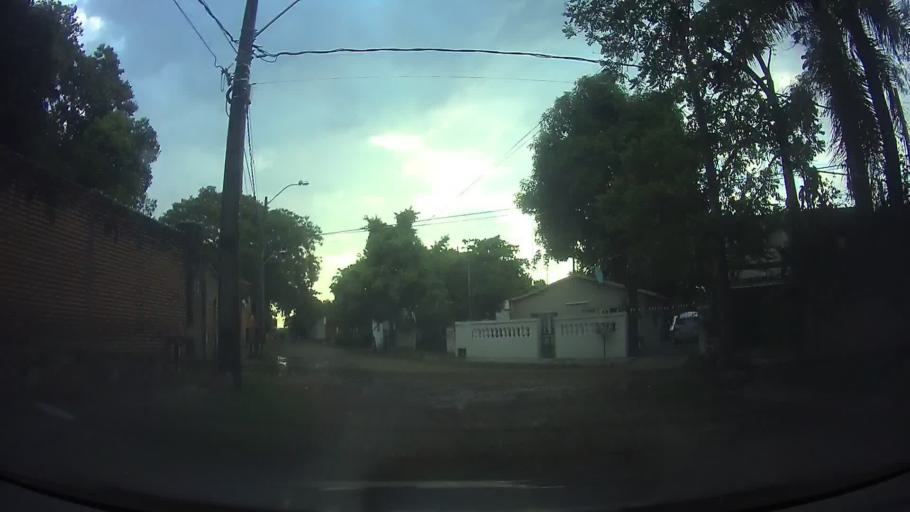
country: PY
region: Asuncion
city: Asuncion
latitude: -25.2649
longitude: -57.5794
